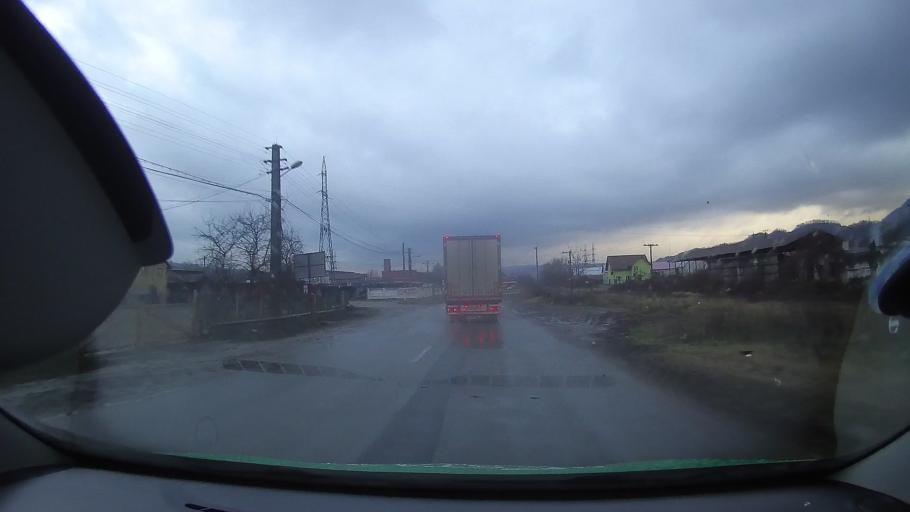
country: RO
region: Hunedoara
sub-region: Municipiul Brad
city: Brad
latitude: 46.1414
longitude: 22.7767
